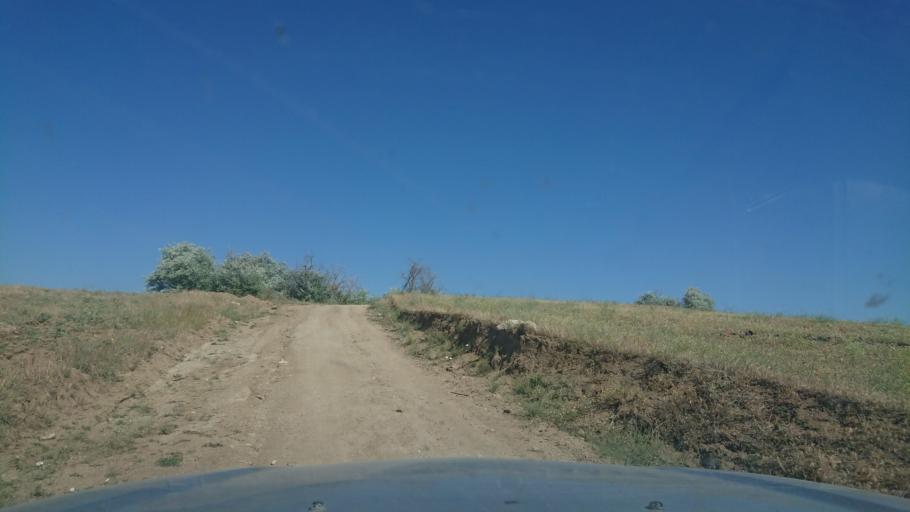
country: TR
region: Aksaray
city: Agacoren
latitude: 38.8455
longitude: 33.9188
